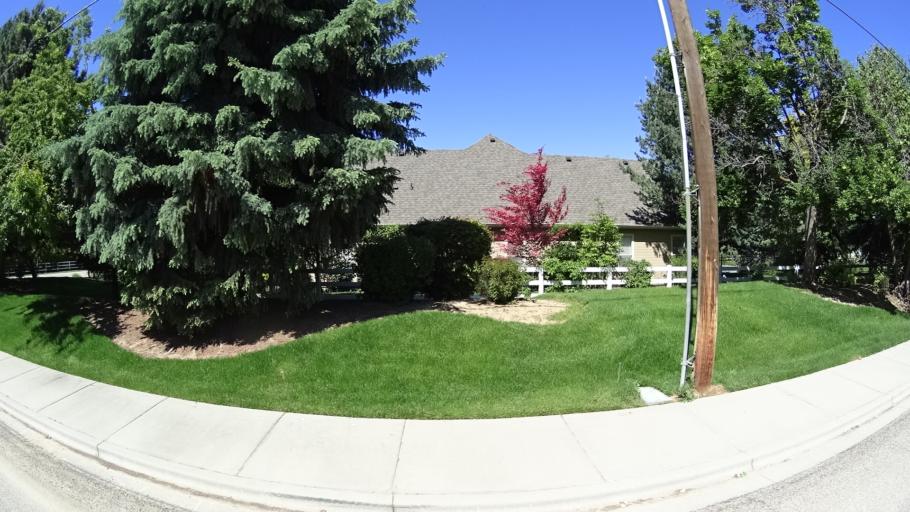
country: US
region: Idaho
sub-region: Ada County
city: Eagle
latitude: 43.6653
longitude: -116.3746
